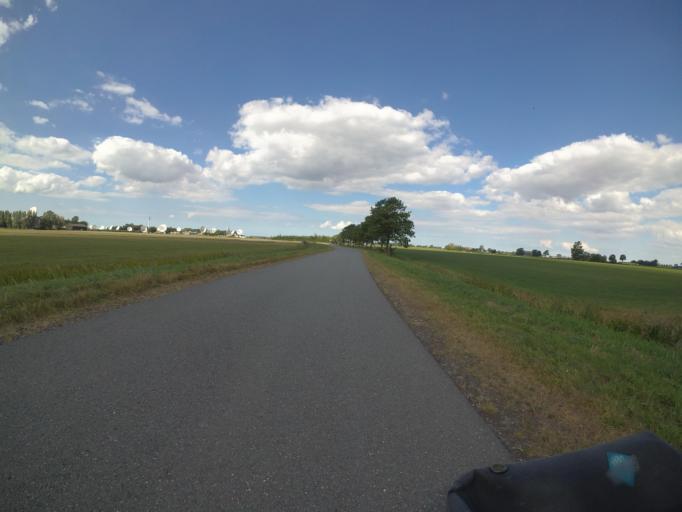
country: NL
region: Friesland
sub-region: Gemeente Kollumerland en Nieuwkruisland
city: Kollum
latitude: 53.2795
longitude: 6.2223
